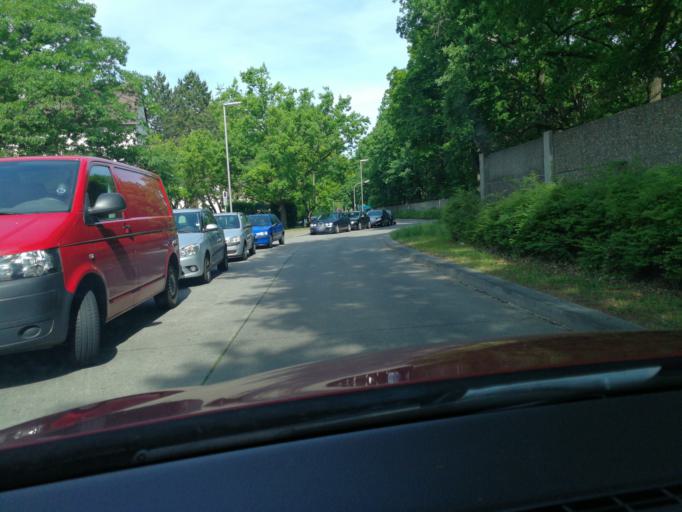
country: DE
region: Berlin
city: Reinickendorf
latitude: 52.5524
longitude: 13.3144
